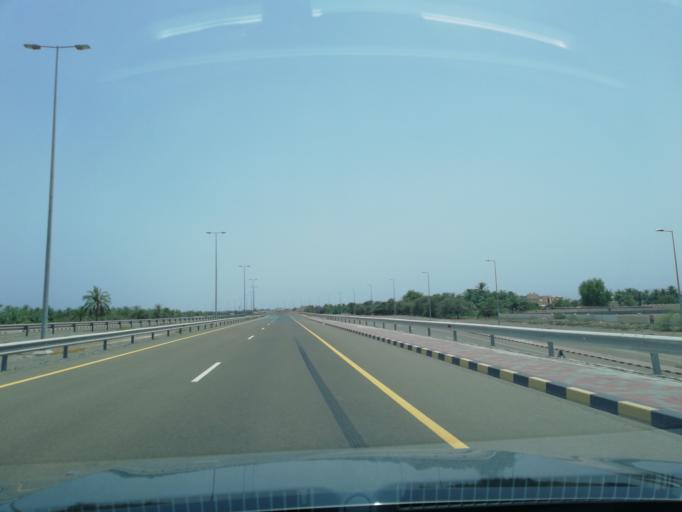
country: OM
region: Al Batinah
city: Shinas
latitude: 24.7978
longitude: 56.4515
